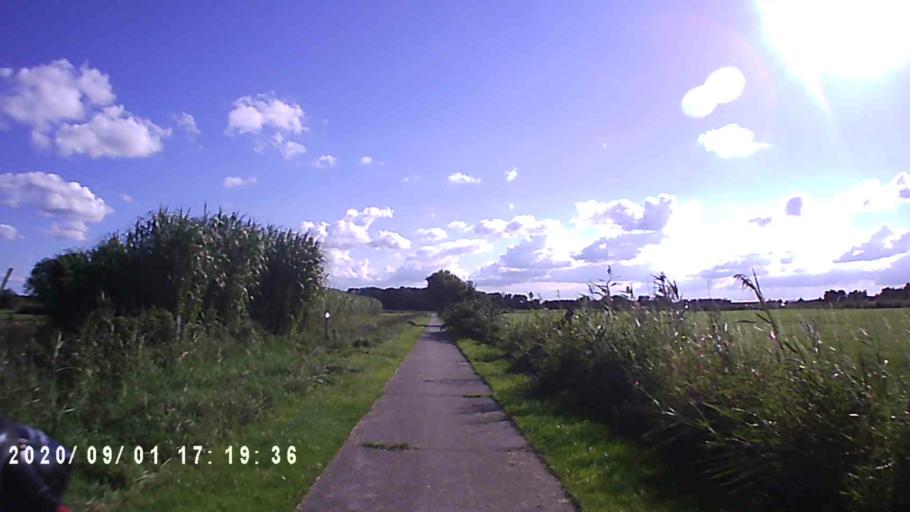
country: NL
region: Groningen
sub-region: Gemeente Haren
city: Haren
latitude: 53.2056
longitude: 6.6656
